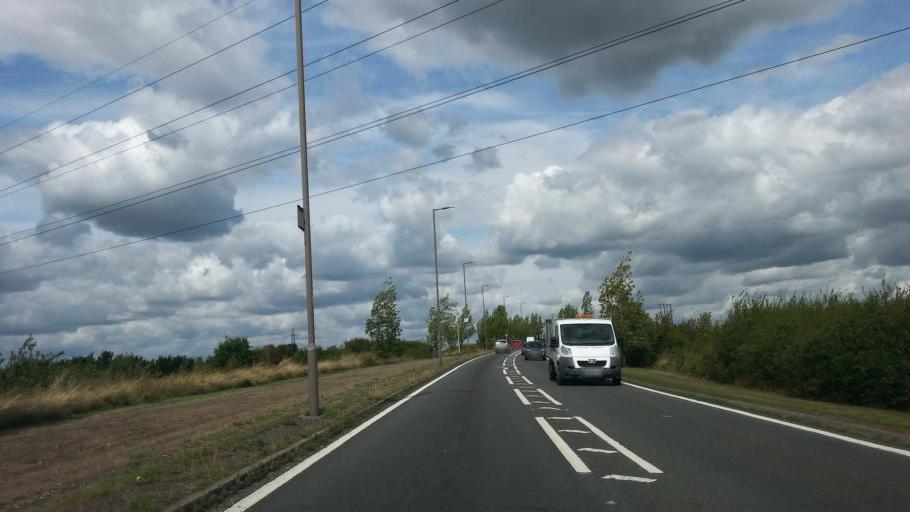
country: GB
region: England
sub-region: Essex
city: South Benfleet
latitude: 51.5513
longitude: 0.5401
